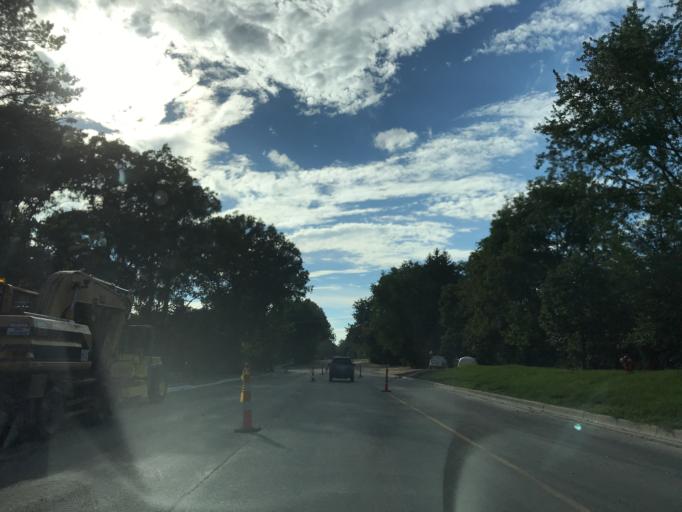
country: US
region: Michigan
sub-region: Oakland County
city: Farmington Hills
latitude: 42.5129
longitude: -83.3924
